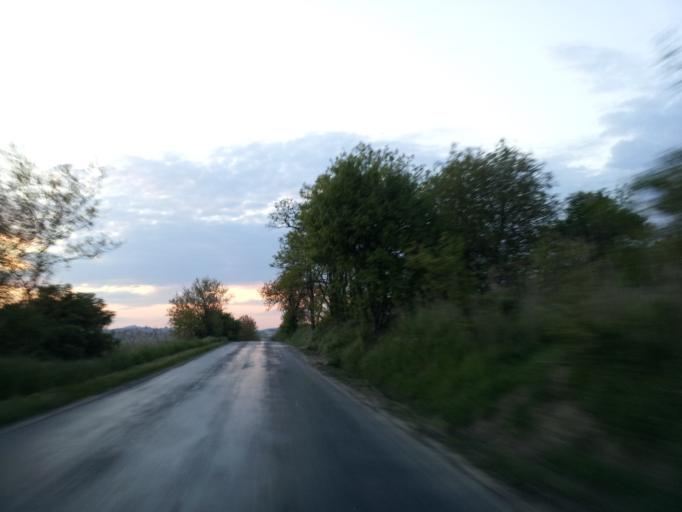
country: HU
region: Komarom-Esztergom
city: Csolnok
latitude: 47.6411
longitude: 18.7251
